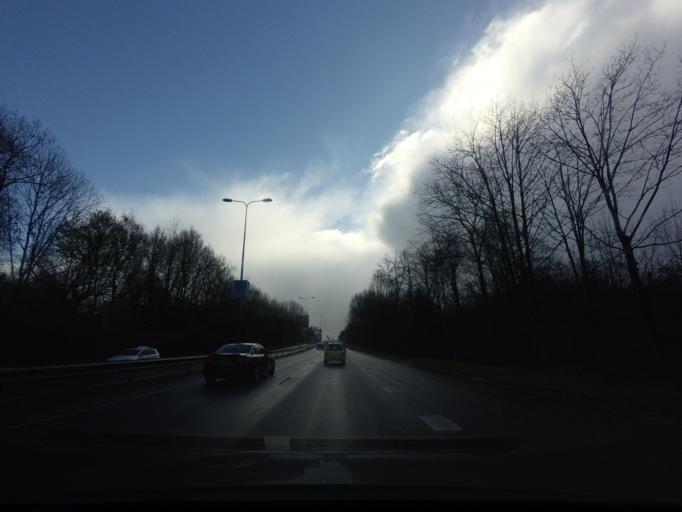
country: NL
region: Groningen
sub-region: Gemeente Groningen
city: Groningen
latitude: 53.2062
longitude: 6.5502
